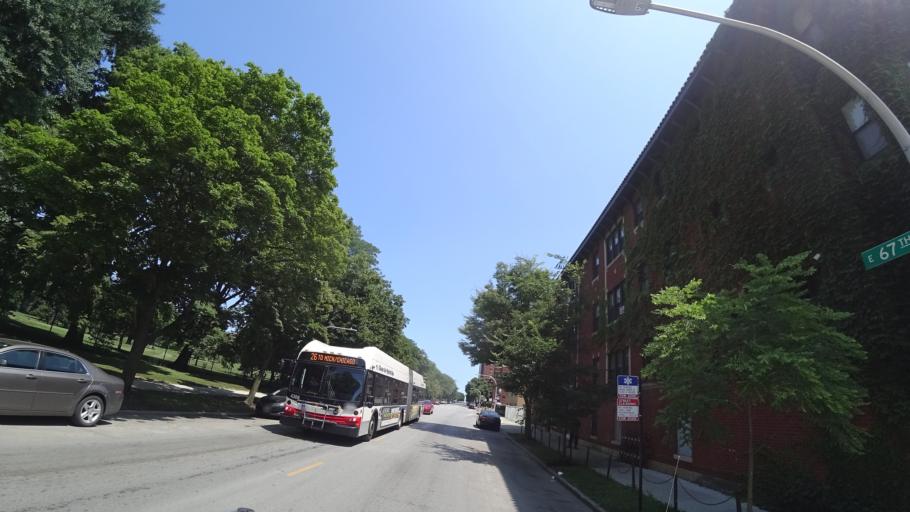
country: US
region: Illinois
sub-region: Cook County
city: Chicago
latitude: 41.7734
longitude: -87.5728
